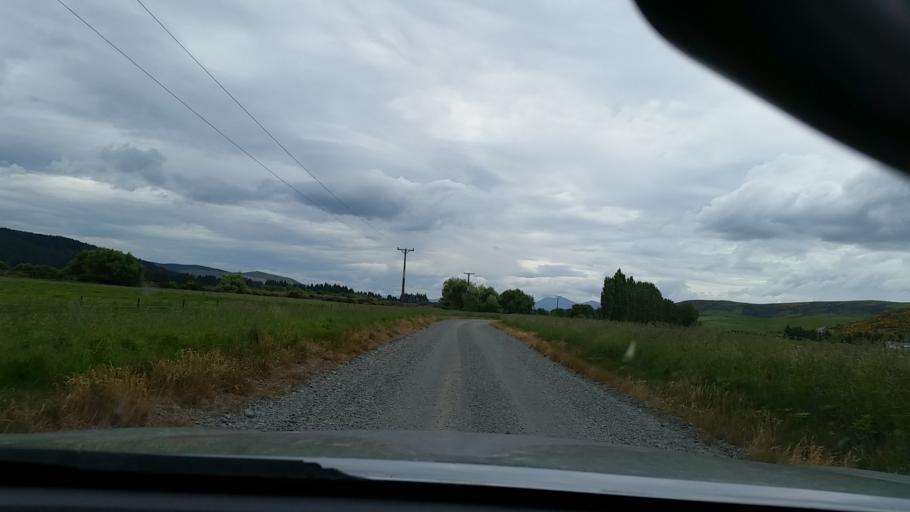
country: NZ
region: Southland
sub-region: Southland District
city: Winton
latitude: -45.8394
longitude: 168.1413
